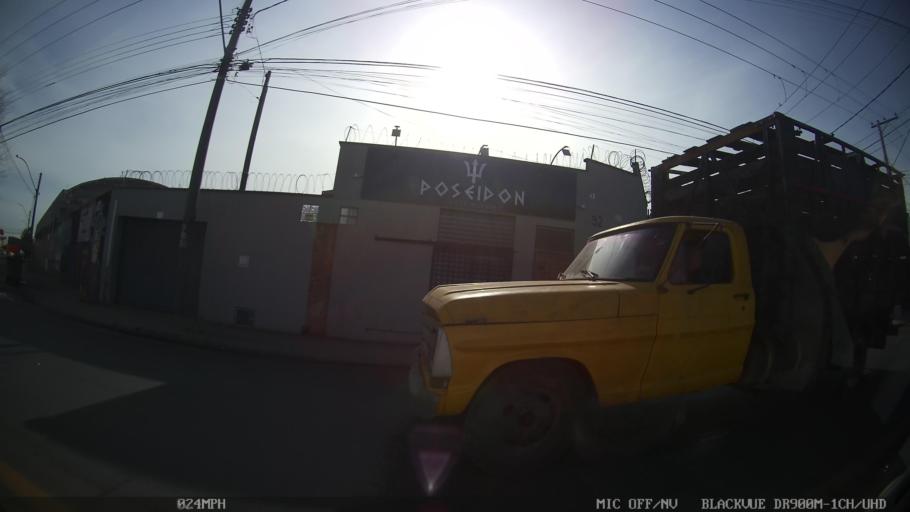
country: BR
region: Sao Paulo
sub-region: Piracicaba
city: Piracicaba
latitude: -22.7528
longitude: -47.6493
